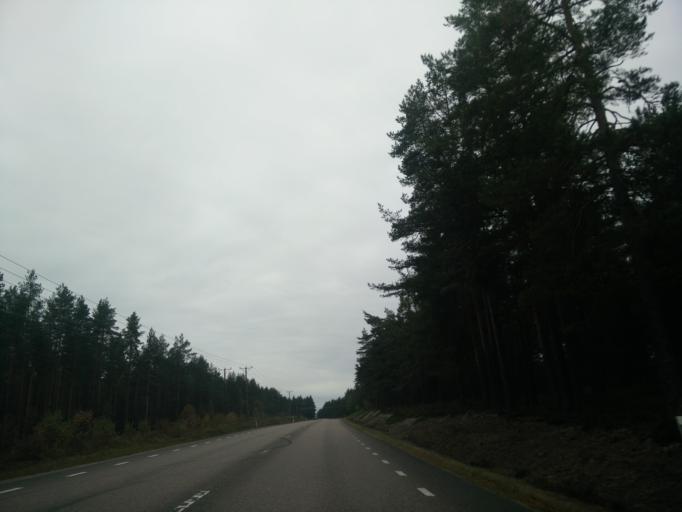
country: SE
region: Gaevleborg
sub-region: Gavle Kommun
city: Gavle
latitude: 60.7777
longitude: 17.1982
